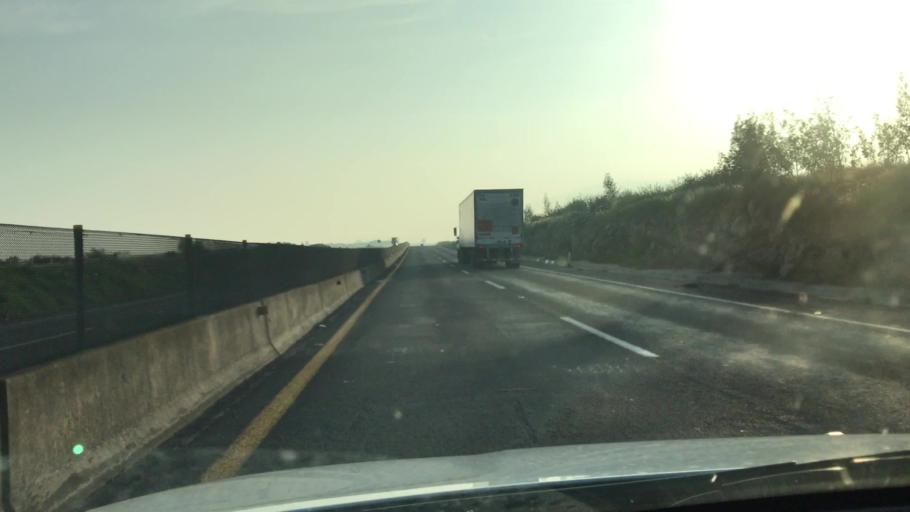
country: MX
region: Jalisco
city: Jalostotitlan
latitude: 21.0987
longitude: -102.4772
